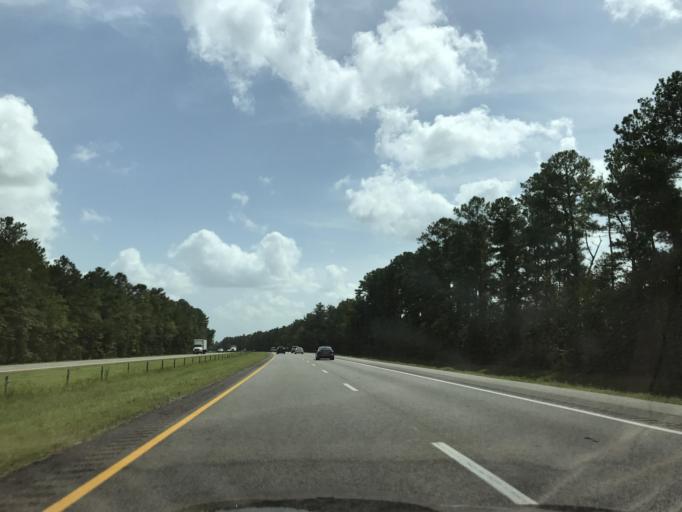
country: US
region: North Carolina
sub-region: Pender County
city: Burgaw
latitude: 34.5342
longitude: -77.8933
